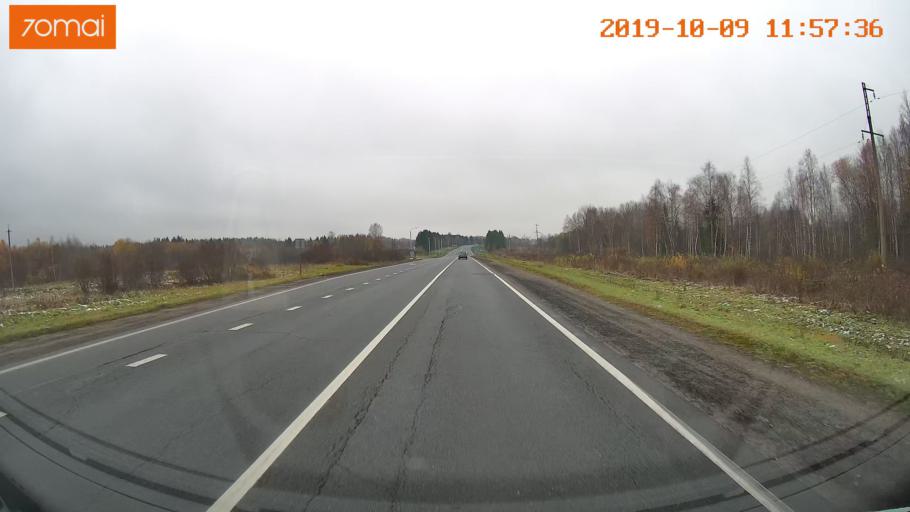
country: RU
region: Vologda
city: Gryazovets
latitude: 58.7300
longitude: 40.2935
